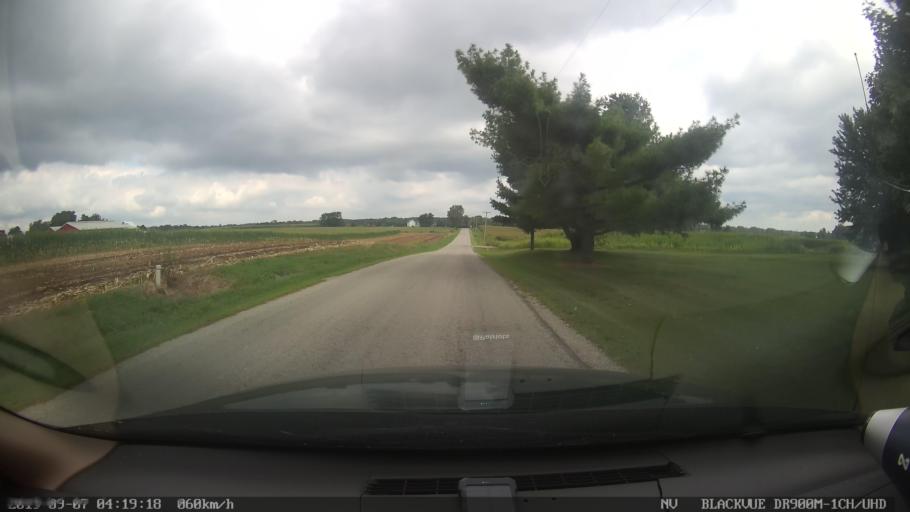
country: US
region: Ohio
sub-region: Knox County
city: Centerburg
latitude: 40.2639
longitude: -82.6627
